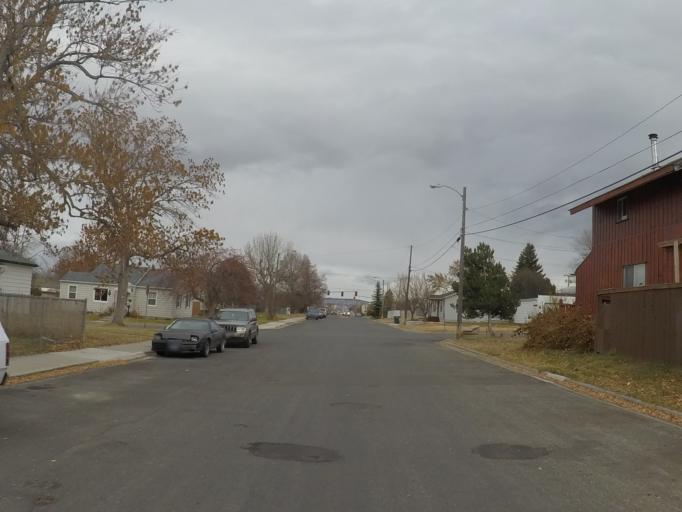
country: US
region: Montana
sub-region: Lewis and Clark County
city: Helena
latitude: 46.5910
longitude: -112.0227
